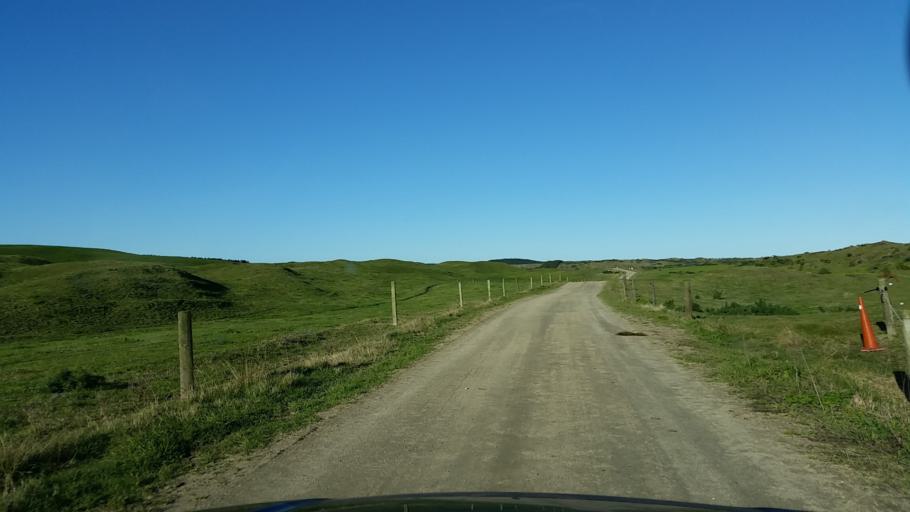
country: NZ
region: Taranaki
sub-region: South Taranaki District
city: Patea
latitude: -39.8366
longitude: 174.6890
